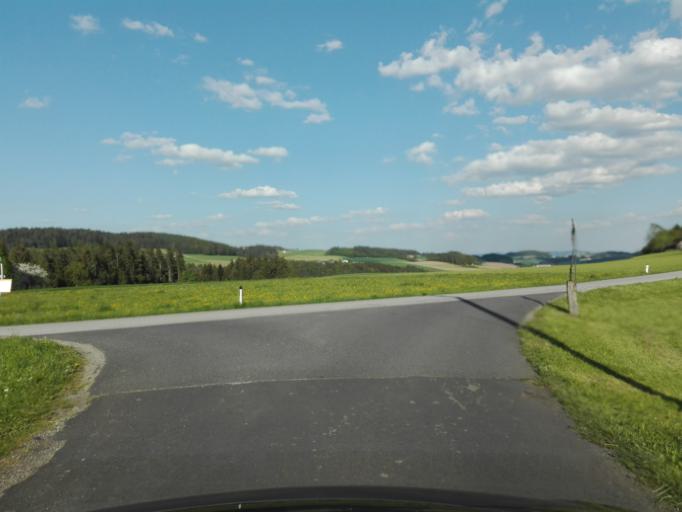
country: AT
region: Upper Austria
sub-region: Politischer Bezirk Rohrbach
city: Atzesberg
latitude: 48.4715
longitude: 13.8763
